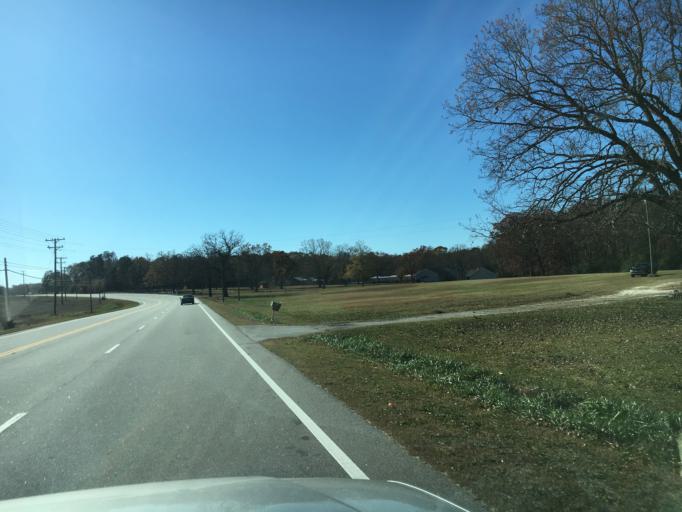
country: US
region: Georgia
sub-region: Hart County
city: Hartwell
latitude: 34.3247
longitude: -82.9762
